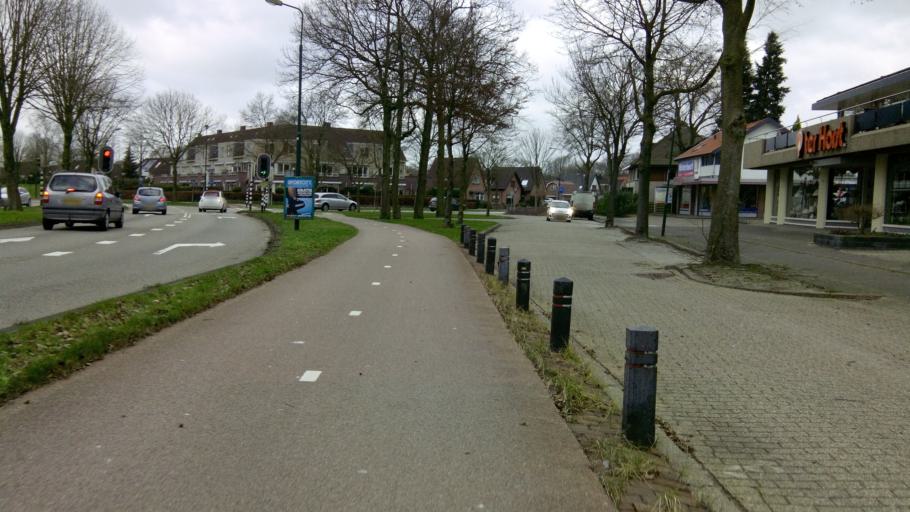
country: NL
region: Utrecht
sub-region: Gemeente Soest
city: Soest
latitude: 52.1656
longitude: 5.3014
